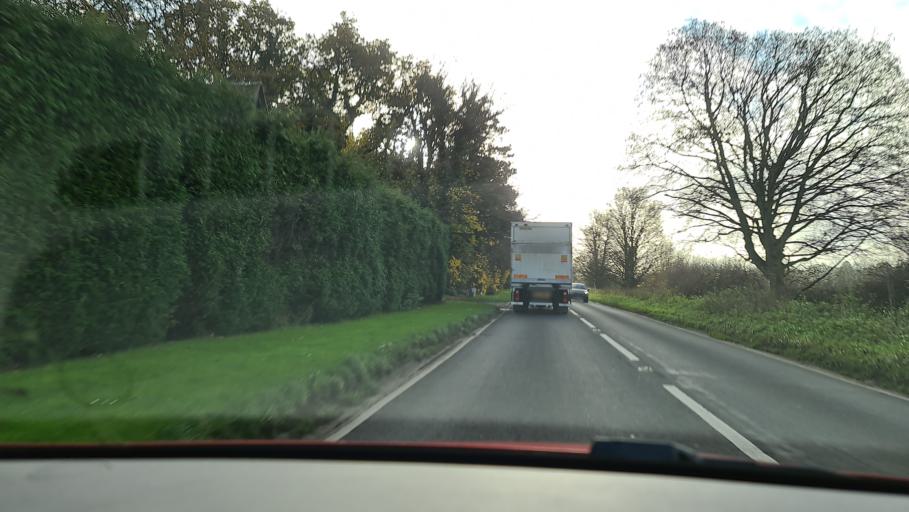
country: GB
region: England
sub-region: Buckinghamshire
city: Great Missenden
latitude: 51.7149
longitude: -0.7154
